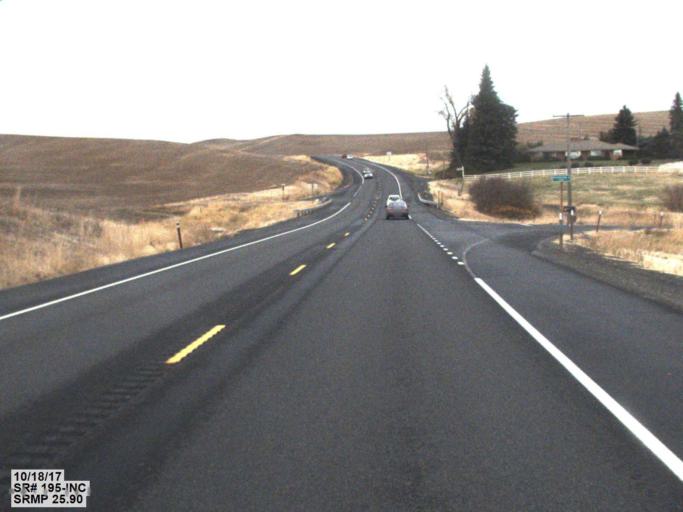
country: US
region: Washington
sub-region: Whitman County
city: Pullman
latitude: 46.7530
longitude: -117.2377
